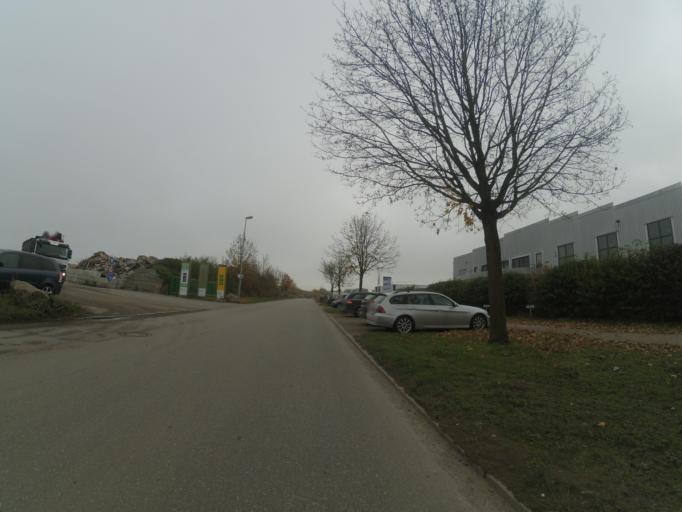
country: DE
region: Baden-Wuerttemberg
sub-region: Tuebingen Region
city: Erbach
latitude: 48.3499
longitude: 9.9335
